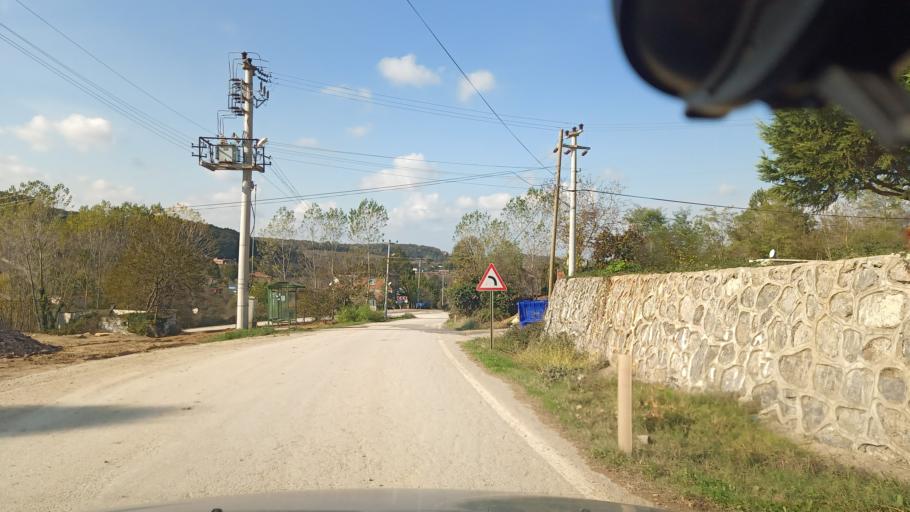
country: TR
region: Sakarya
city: Ferizli
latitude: 41.1063
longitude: 30.4769
